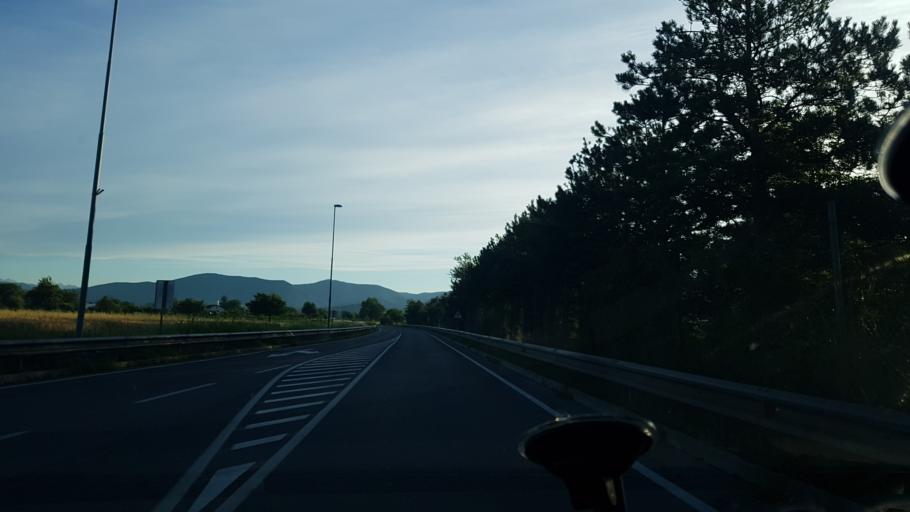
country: SI
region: Sempeter-Vrtojba
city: Vrtojba
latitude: 45.9100
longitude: 13.6269
